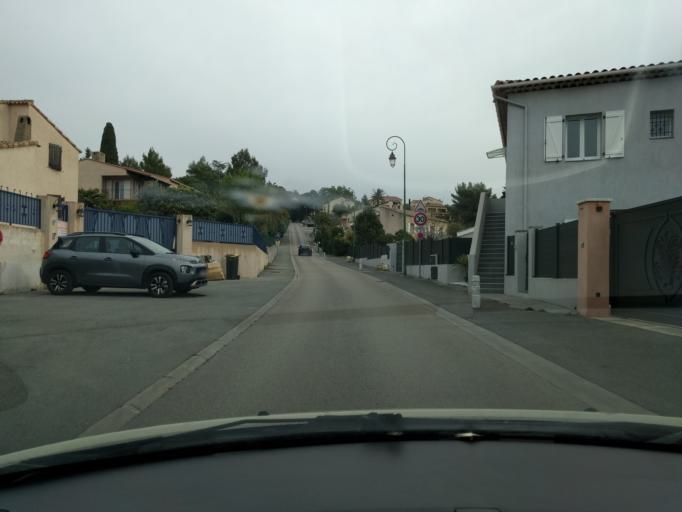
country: FR
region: Provence-Alpes-Cote d'Azur
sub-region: Departement des Alpes-Maritimes
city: La Roquette-sur-Siagne
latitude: 43.5792
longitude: 6.9504
